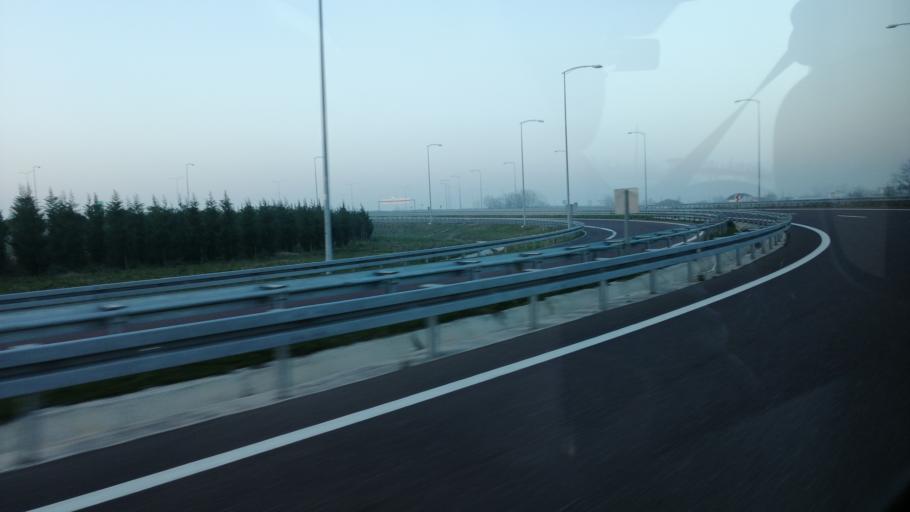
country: TR
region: Yalova
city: Altinova
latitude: 40.6976
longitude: 29.4890
